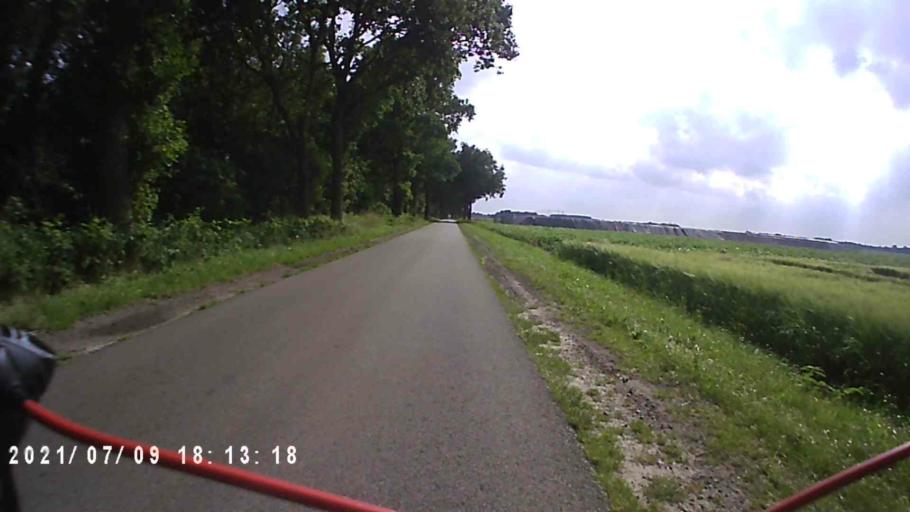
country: NL
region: Groningen
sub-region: Gemeente Pekela
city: Oude Pekela
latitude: 53.0638
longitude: 7.0266
